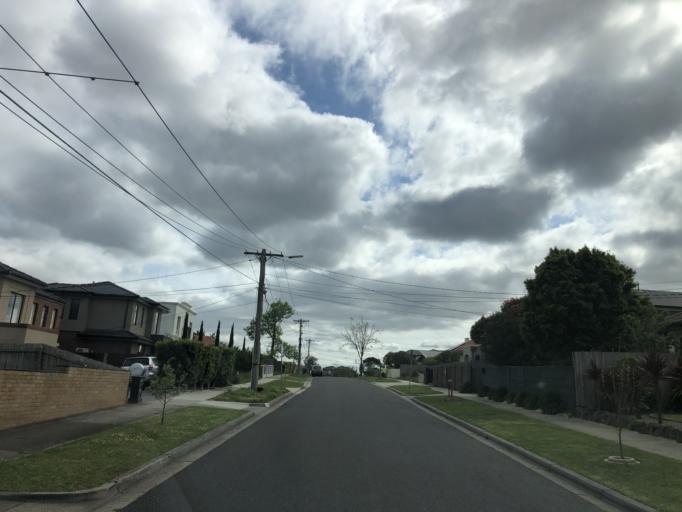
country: AU
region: Victoria
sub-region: Monash
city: Chadstone
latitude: -37.8771
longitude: 145.0948
